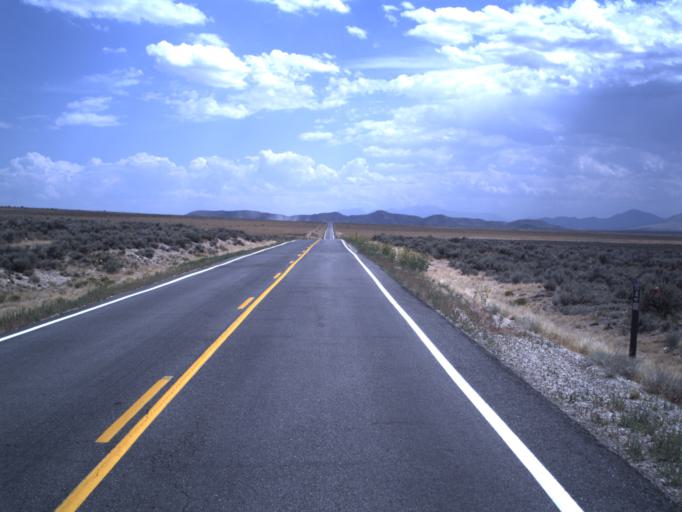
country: US
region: Utah
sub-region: Utah County
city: Eagle Mountain
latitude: 40.2765
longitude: -112.2522
